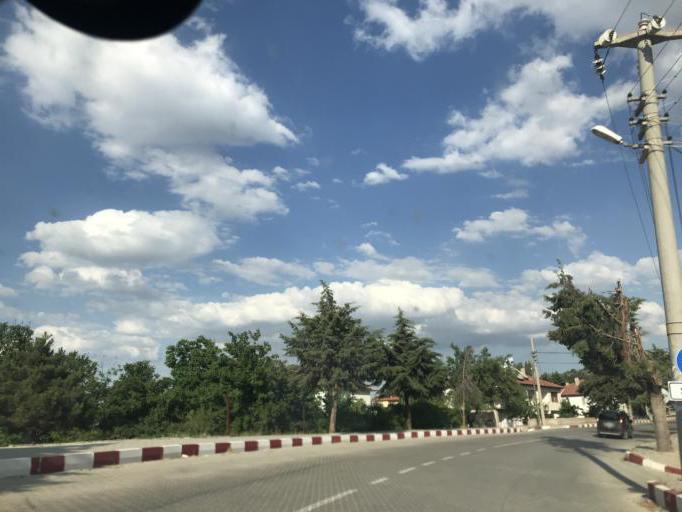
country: TR
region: Burdur
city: Yesilova
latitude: 37.5042
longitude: 29.7576
